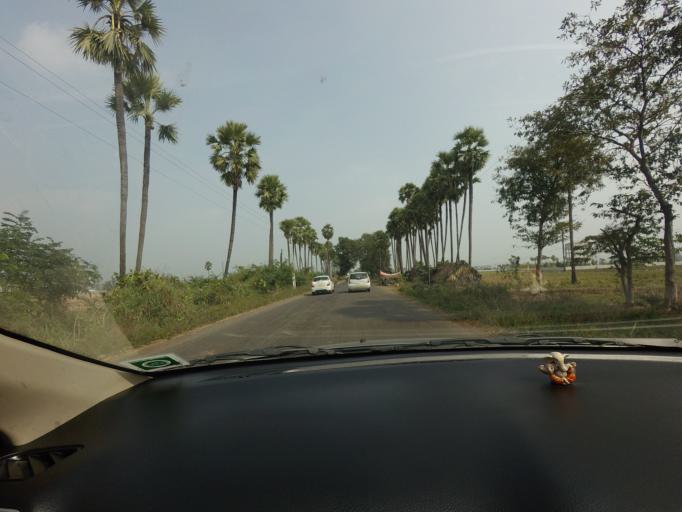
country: IN
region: Andhra Pradesh
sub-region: Krishna
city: Kankipadu
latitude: 16.4541
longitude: 80.7895
